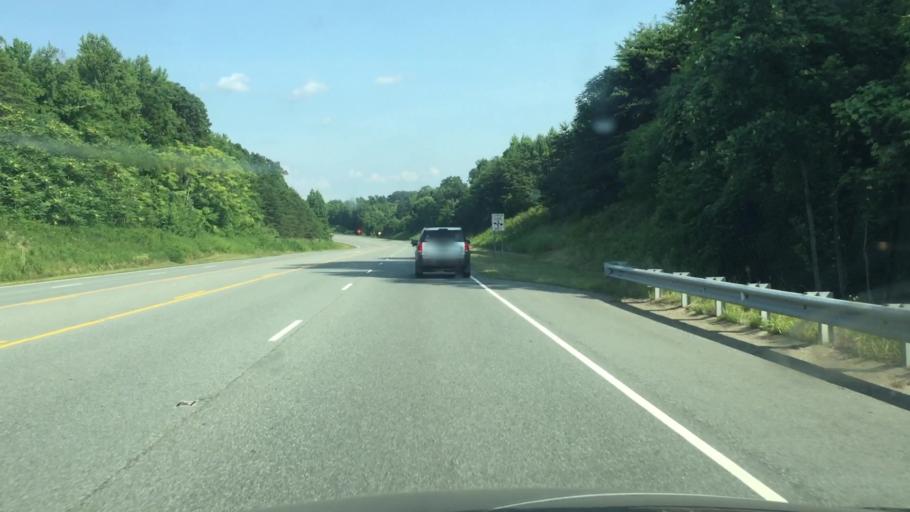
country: US
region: North Carolina
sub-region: Rockingham County
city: Reidsville
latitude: 36.3665
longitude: -79.6424
